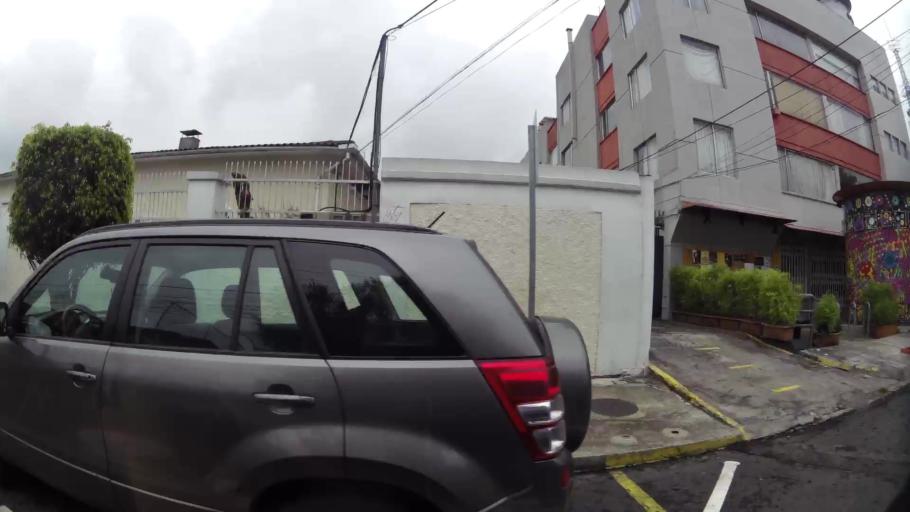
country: EC
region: Pichincha
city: Quito
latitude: -0.2077
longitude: -78.4838
